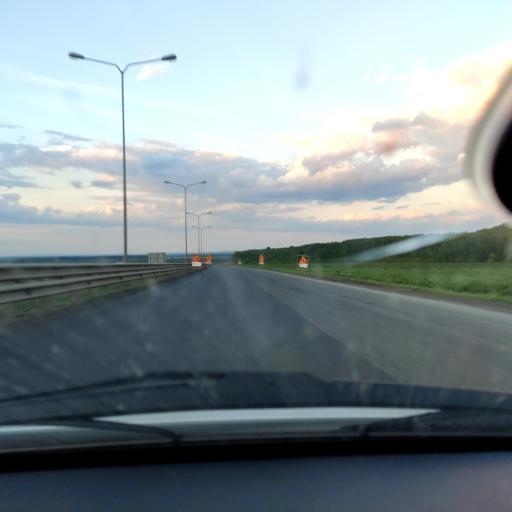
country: RU
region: Bashkortostan
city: Kushnarenkovo
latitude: 55.0647
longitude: 55.3296
